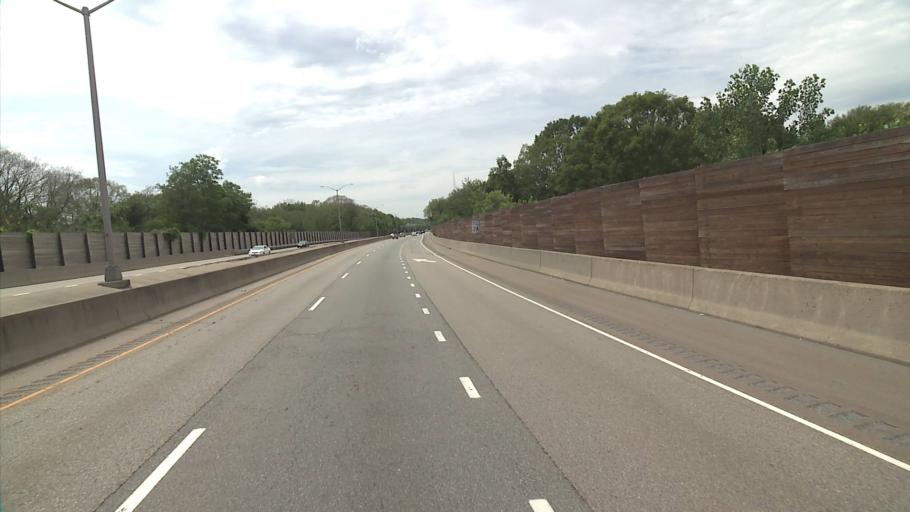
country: US
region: Connecticut
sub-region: New London County
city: Norwich
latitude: 41.4809
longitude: -72.0886
